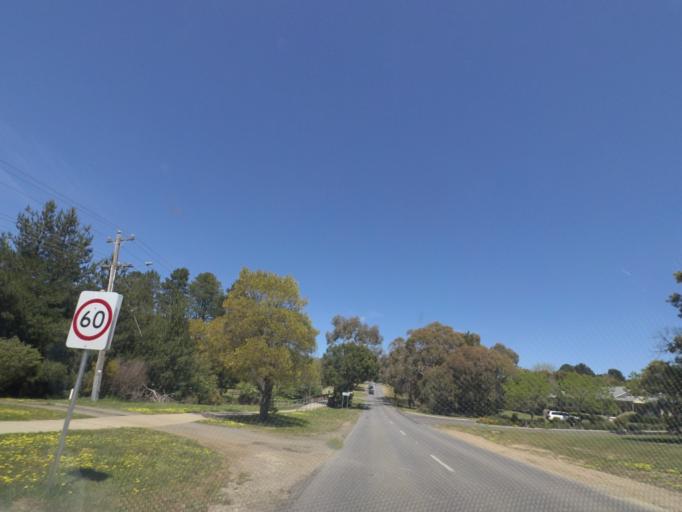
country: AU
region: Victoria
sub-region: Hume
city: Sunbury
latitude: -37.4967
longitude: 144.5896
